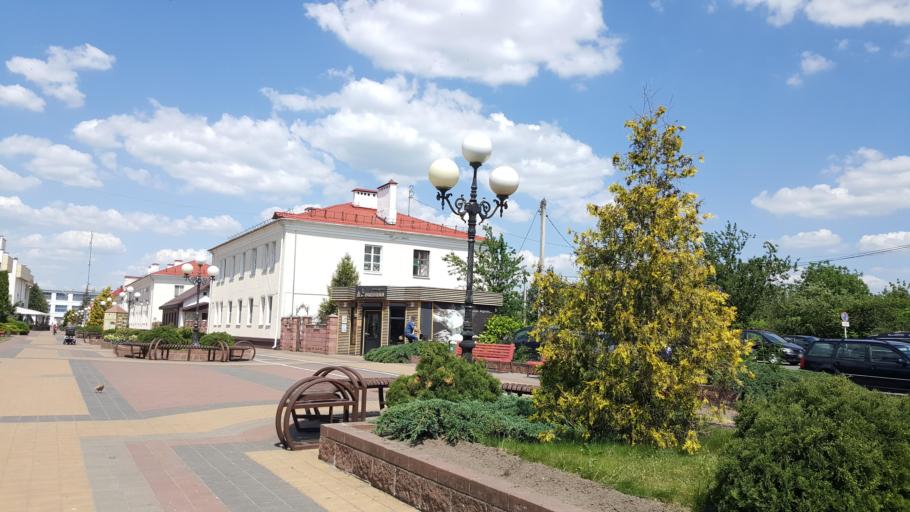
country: BY
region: Brest
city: Kobryn
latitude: 52.2091
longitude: 24.3553
